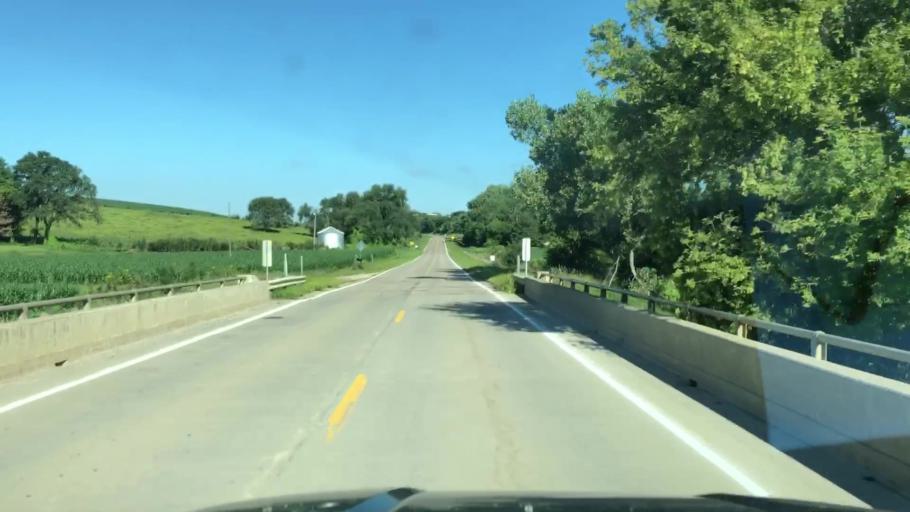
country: US
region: Iowa
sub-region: Woodbury County
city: Sergeant Bluff
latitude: 42.4169
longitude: -96.2634
